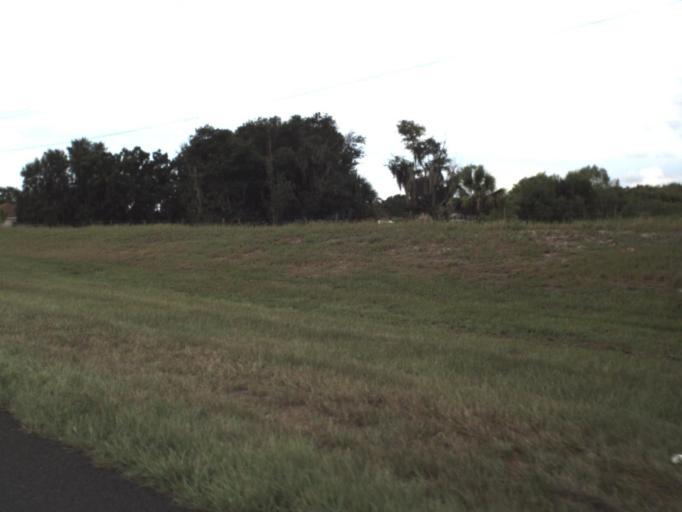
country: US
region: Florida
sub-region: Polk County
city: Bartow
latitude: 27.8328
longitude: -81.8233
